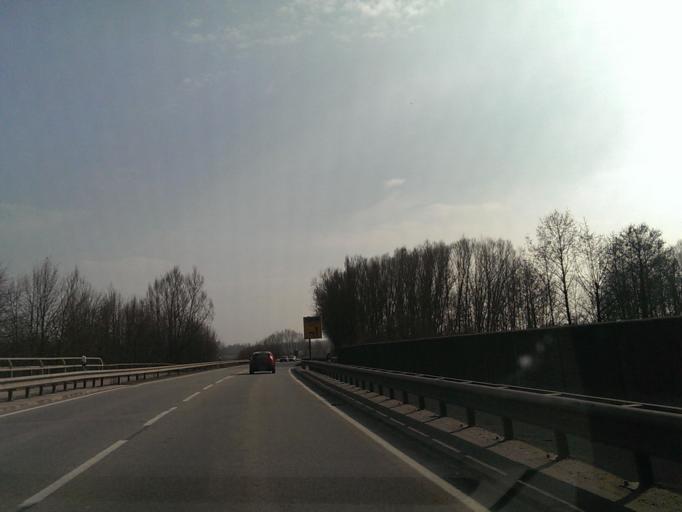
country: DE
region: Bavaria
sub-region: Upper Palatinate
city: Donaustauf
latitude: 49.0201
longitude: 12.2159
